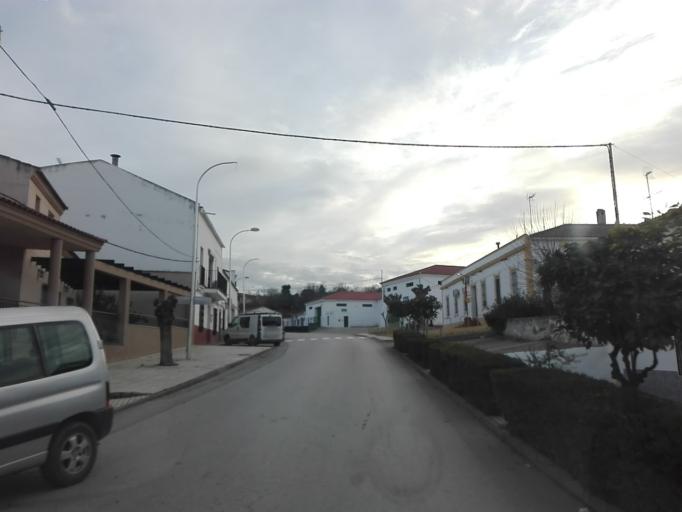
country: ES
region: Extremadura
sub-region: Provincia de Badajoz
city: Usagre
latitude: 38.3548
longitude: -6.1708
